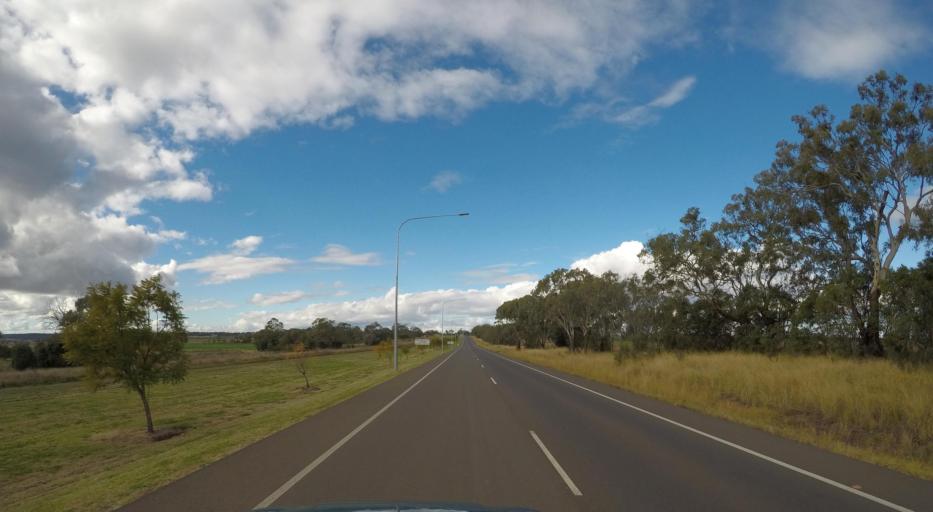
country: AU
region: Queensland
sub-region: Toowoomba
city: Westbrook
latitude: -27.7204
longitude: 151.6132
